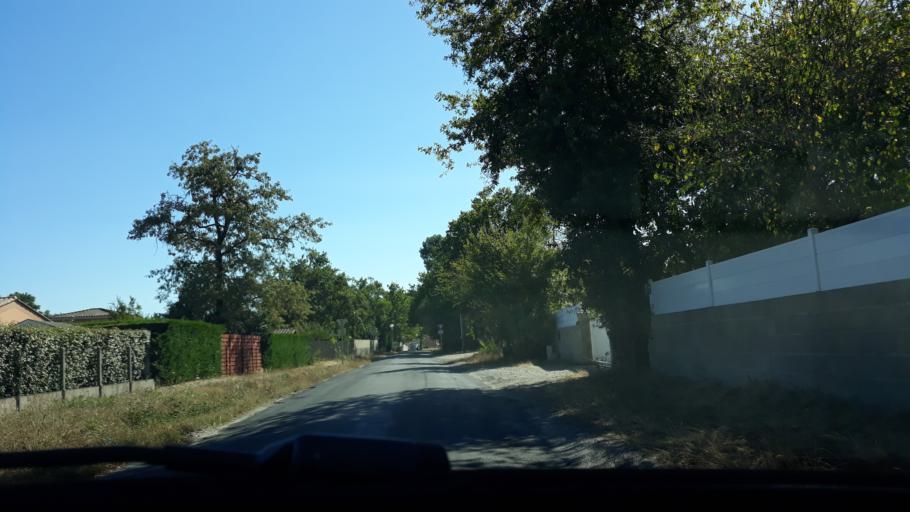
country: FR
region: Aquitaine
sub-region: Departement de la Gironde
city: Leognan
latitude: 44.7392
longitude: -0.6112
